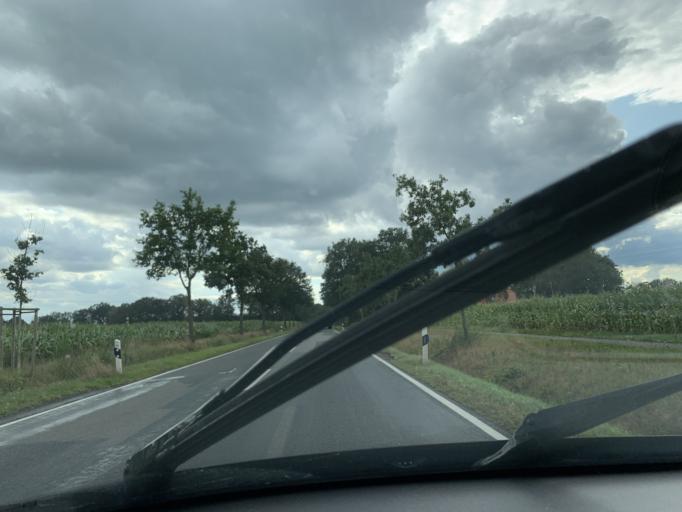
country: DE
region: Lower Saxony
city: Wiefelstede
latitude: 53.2958
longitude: 8.0457
